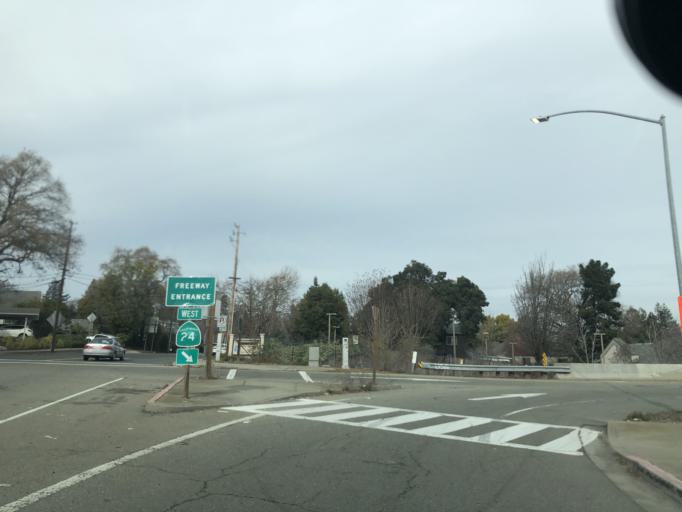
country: US
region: California
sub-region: Contra Costa County
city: Walnut Creek
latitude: 37.9067
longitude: -122.0704
